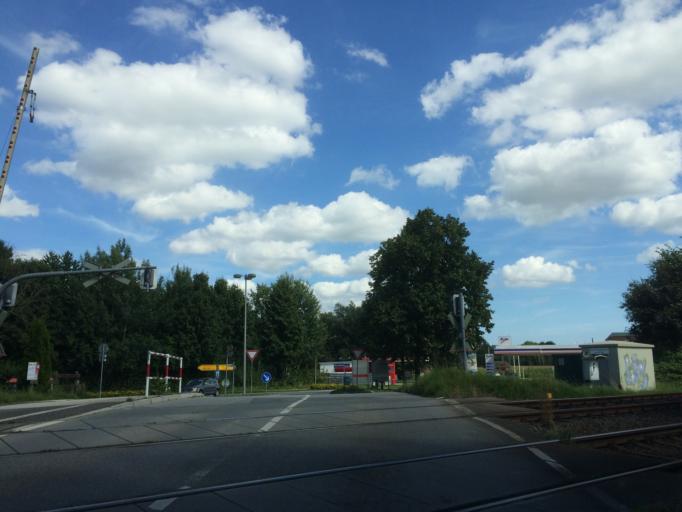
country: DE
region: Schleswig-Holstein
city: Malente
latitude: 54.1635
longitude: 10.5650
